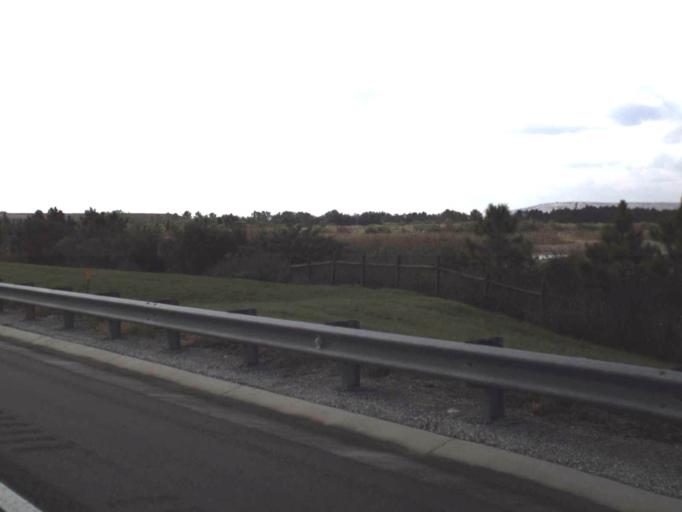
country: US
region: Florida
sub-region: Polk County
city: Fussels Corner
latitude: 28.0349
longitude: -81.8332
